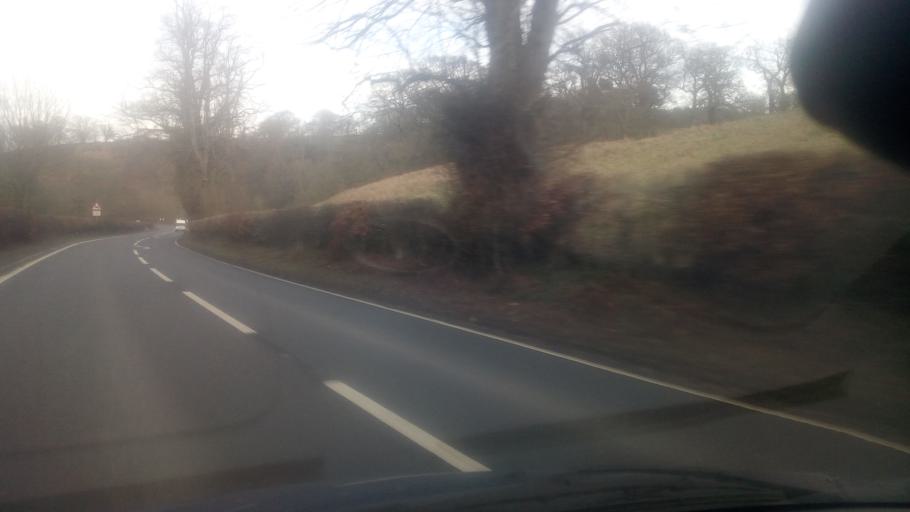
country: GB
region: Scotland
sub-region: The Scottish Borders
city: Jedburgh
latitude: 55.4614
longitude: -2.5562
